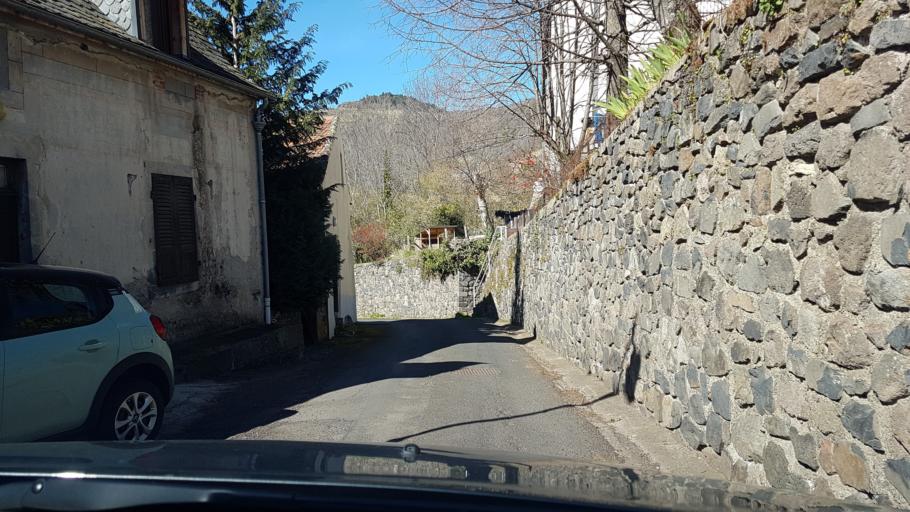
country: FR
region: Auvergne
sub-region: Departement du Puy-de-Dome
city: Aydat
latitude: 45.5444
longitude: 3.0006
